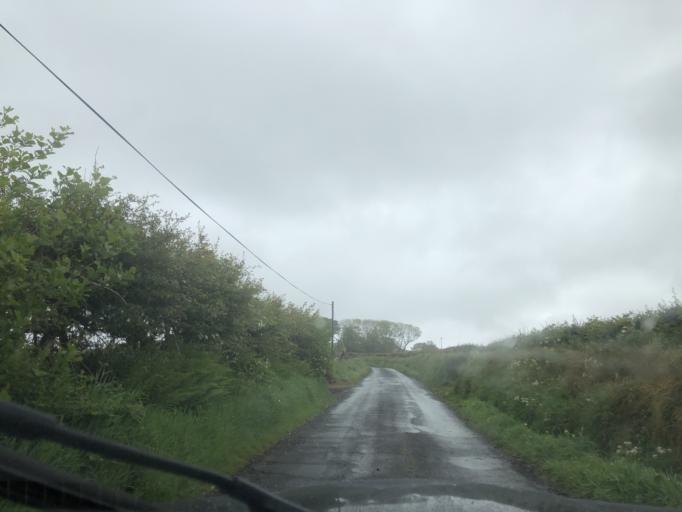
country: GB
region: Northern Ireland
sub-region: Moyle District
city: Ballycastle
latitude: 55.2098
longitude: -6.1610
